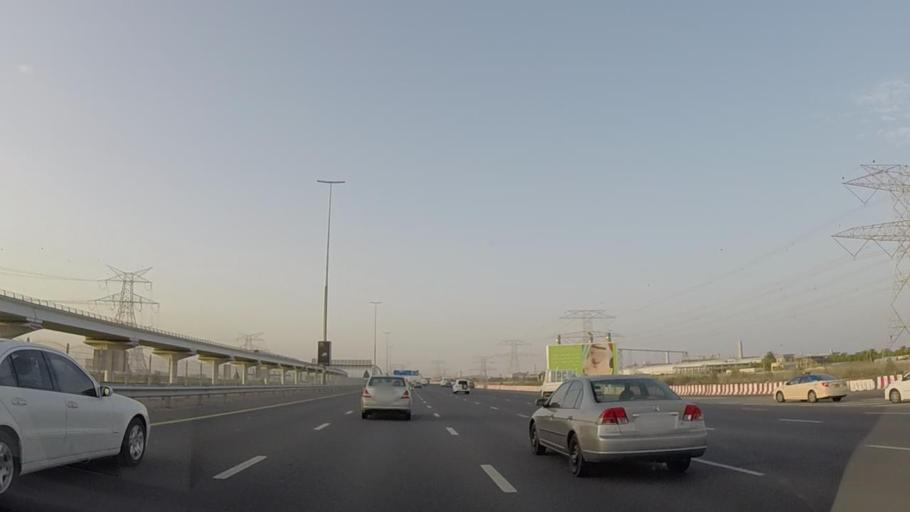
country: AE
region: Dubai
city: Dubai
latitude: 25.0362
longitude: 55.1076
